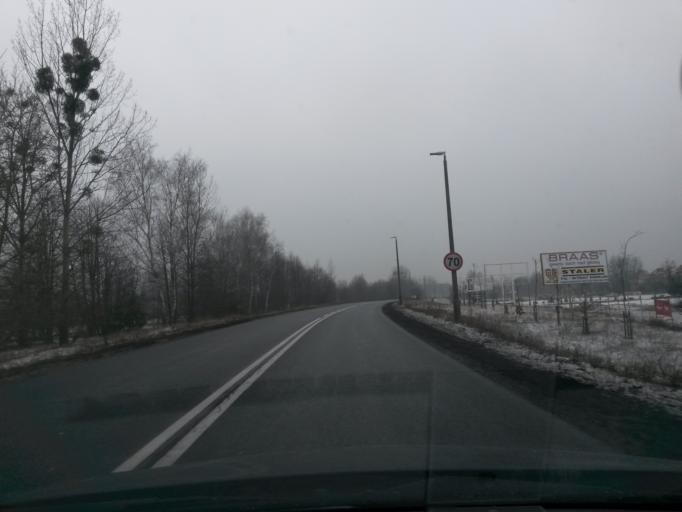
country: PL
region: Kujawsko-Pomorskie
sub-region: Torun
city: Torun
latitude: 52.9756
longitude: 18.5637
